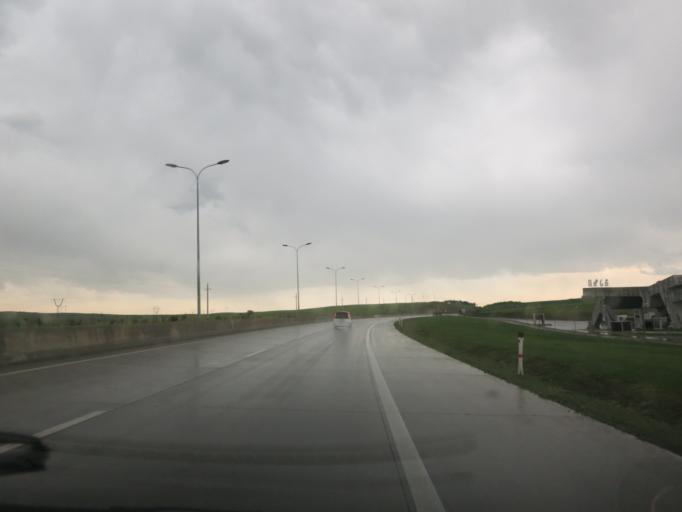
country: GE
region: Shida Kartli
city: Gori
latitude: 42.0174
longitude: 44.0251
